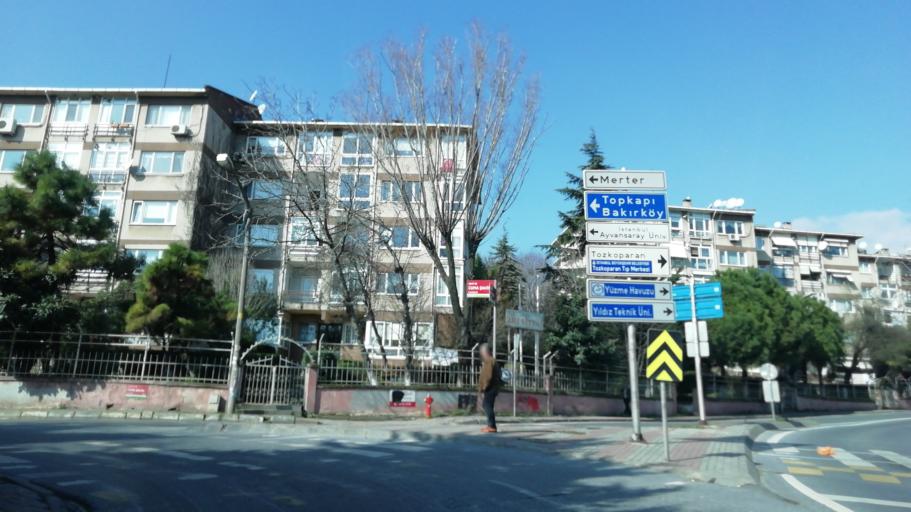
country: TR
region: Istanbul
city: guengoeren merter
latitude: 41.0113
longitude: 28.8968
